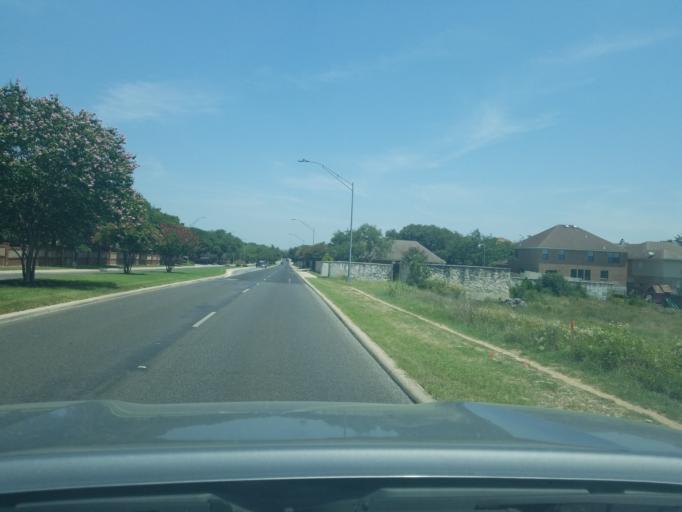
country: US
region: Texas
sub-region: Bexar County
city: Hollywood Park
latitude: 29.6478
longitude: -98.4948
